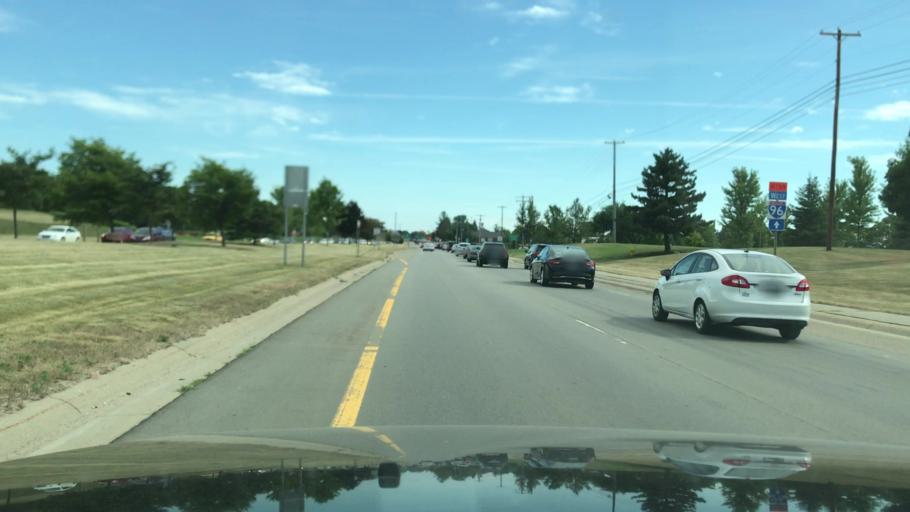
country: US
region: Michigan
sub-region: Kent County
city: East Grand Rapids
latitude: 42.9812
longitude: -85.5907
